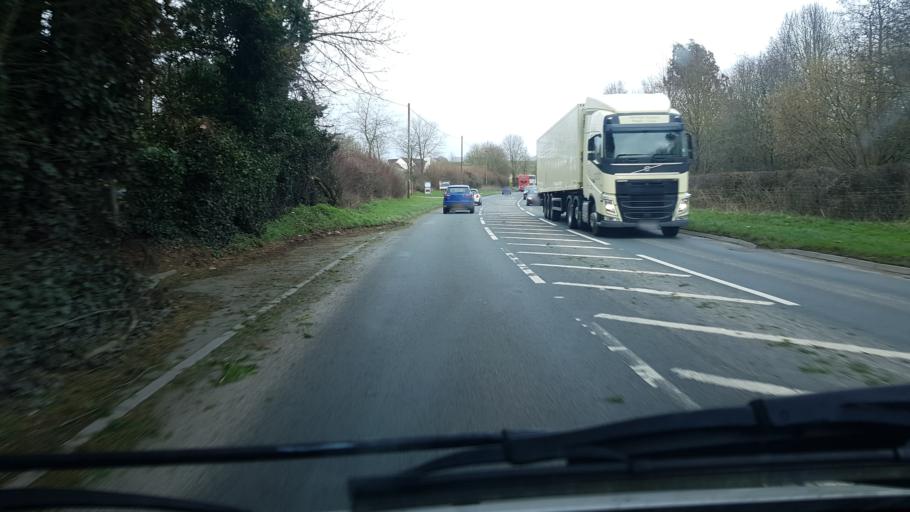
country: GB
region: England
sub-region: Wiltshire
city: Fyfield
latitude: 51.4198
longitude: -1.7720
